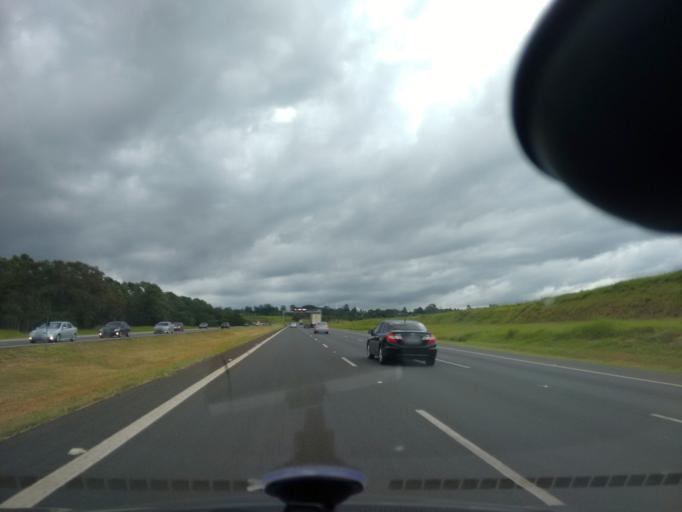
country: BR
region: Sao Paulo
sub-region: Hortolandia
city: Hortolandia
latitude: -22.9144
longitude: -47.1592
